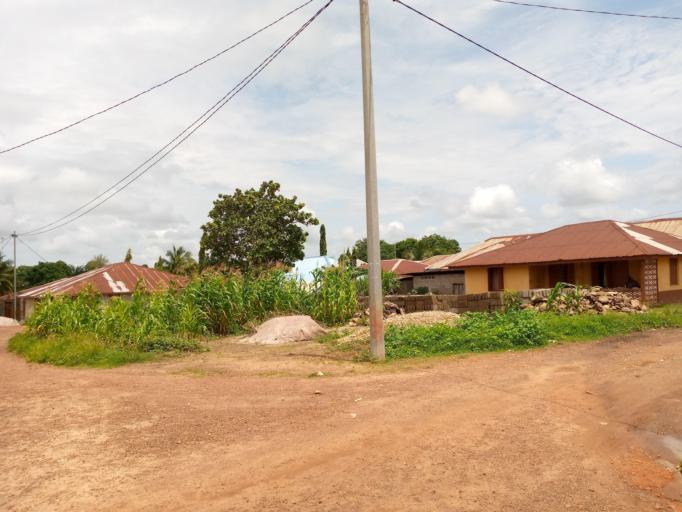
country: SL
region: Northern Province
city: Magburaka
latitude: 8.7249
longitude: -11.9360
